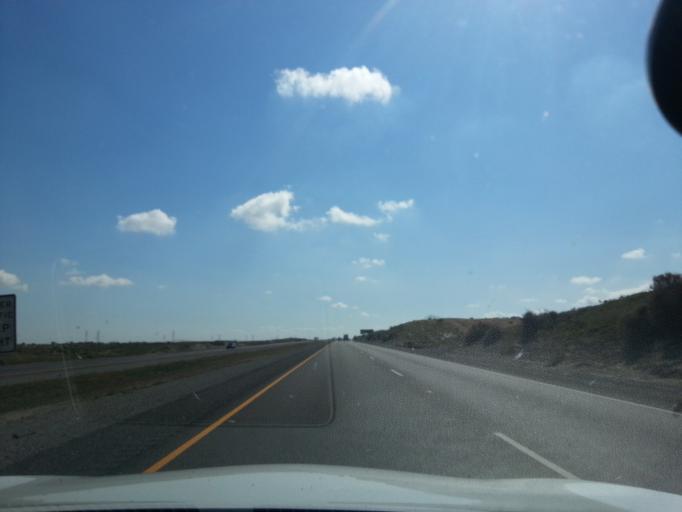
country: US
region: California
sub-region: Fresno County
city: Mendota
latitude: 36.5238
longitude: -120.4789
